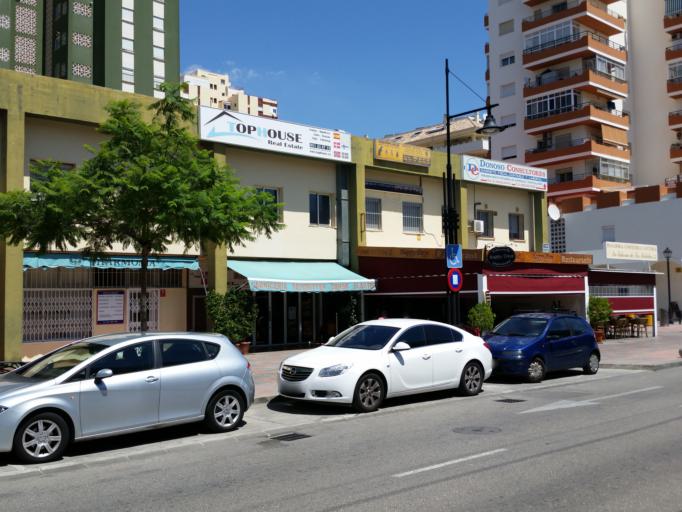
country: ES
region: Andalusia
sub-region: Provincia de Malaga
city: Fuengirola
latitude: 36.5514
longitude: -4.6170
